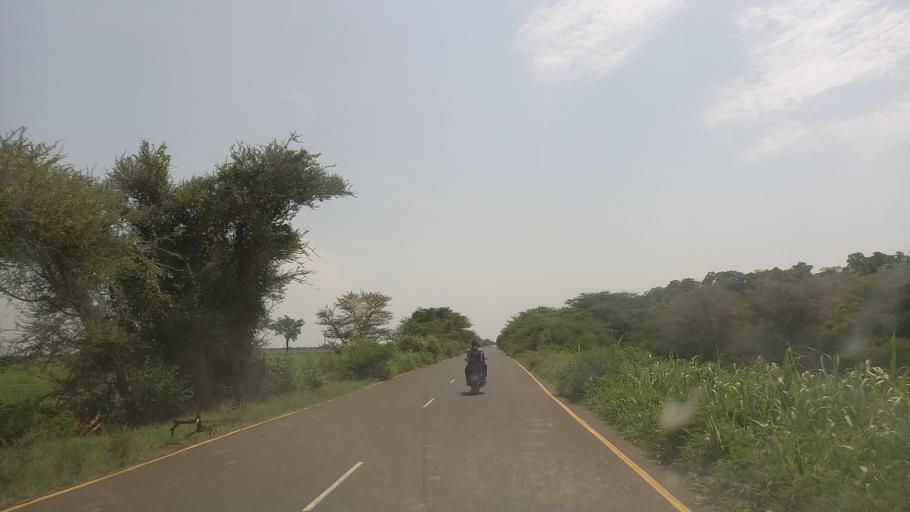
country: ET
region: Gambela
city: Gambela
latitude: 8.2842
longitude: 34.2145
